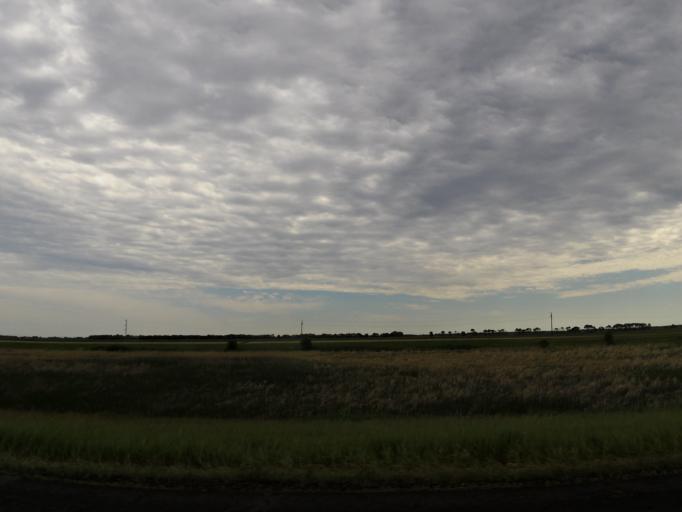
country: US
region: North Dakota
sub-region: Walsh County
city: Grafton
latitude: 48.3028
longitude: -97.1890
